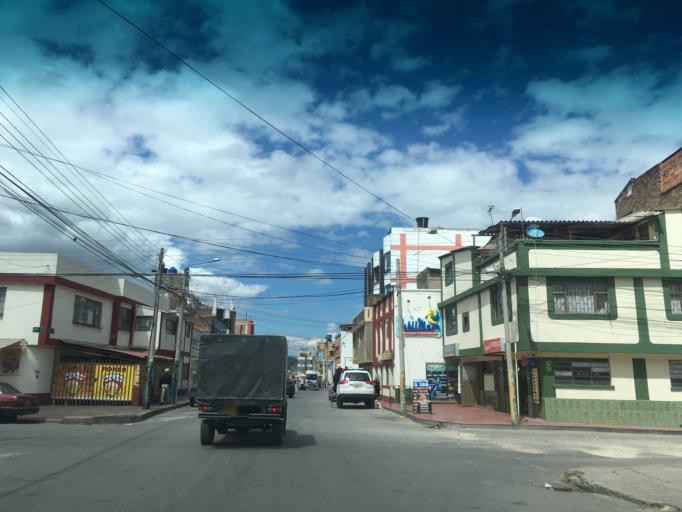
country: CO
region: Boyaca
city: Sogamoso
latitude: 5.7163
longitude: -72.9331
